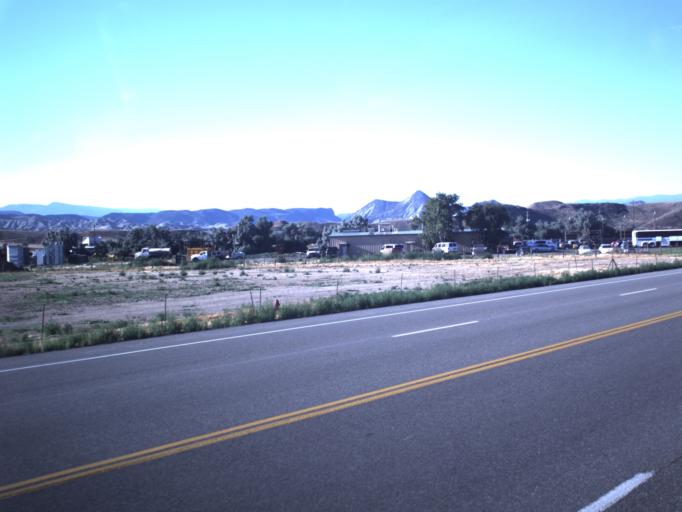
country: US
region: Utah
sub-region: Sevier County
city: Salina
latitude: 38.9510
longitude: -111.8774
